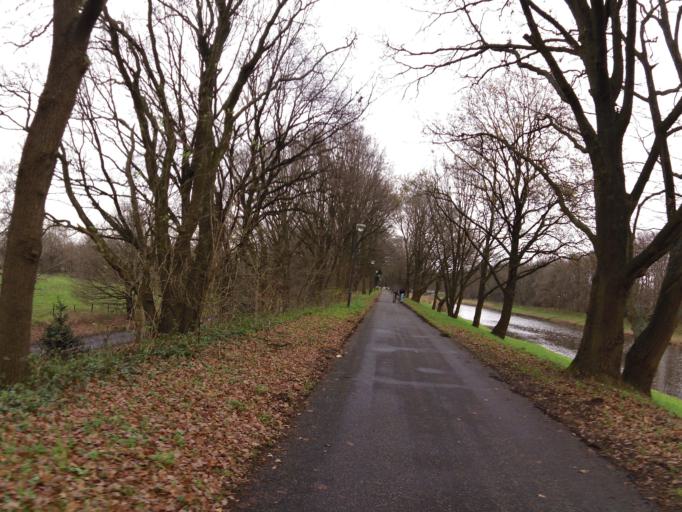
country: NL
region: North Brabant
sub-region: Gemeente Vught
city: Vught
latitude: 51.6699
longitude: 5.2804
